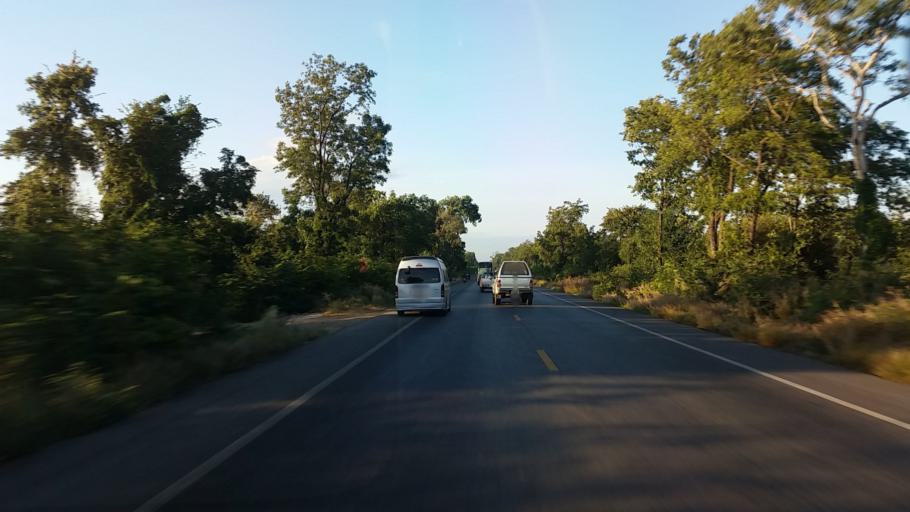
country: TH
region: Lop Buri
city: Chai Badan
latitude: 15.2436
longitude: 101.1676
